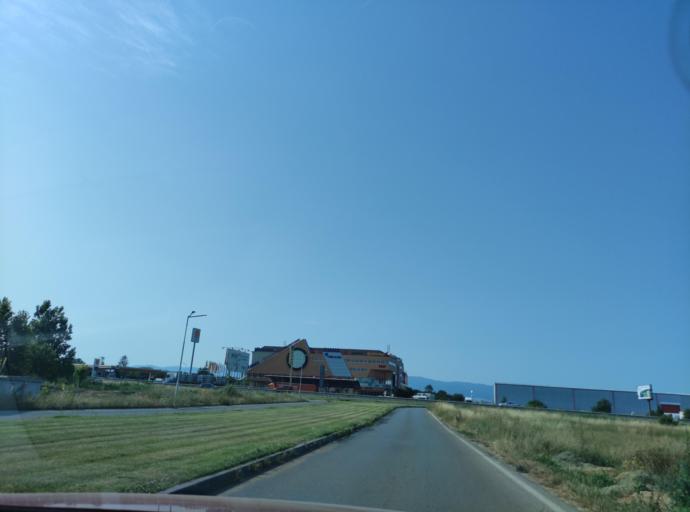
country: BG
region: Sofia-Capital
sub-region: Stolichna Obshtina
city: Bukhovo
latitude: 42.7084
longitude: 23.4560
